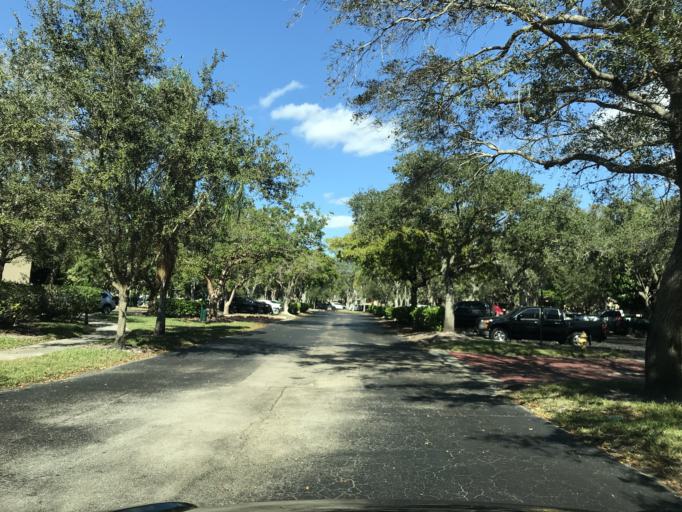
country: US
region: Florida
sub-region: Broward County
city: Plantation
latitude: 26.1308
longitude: -80.2675
